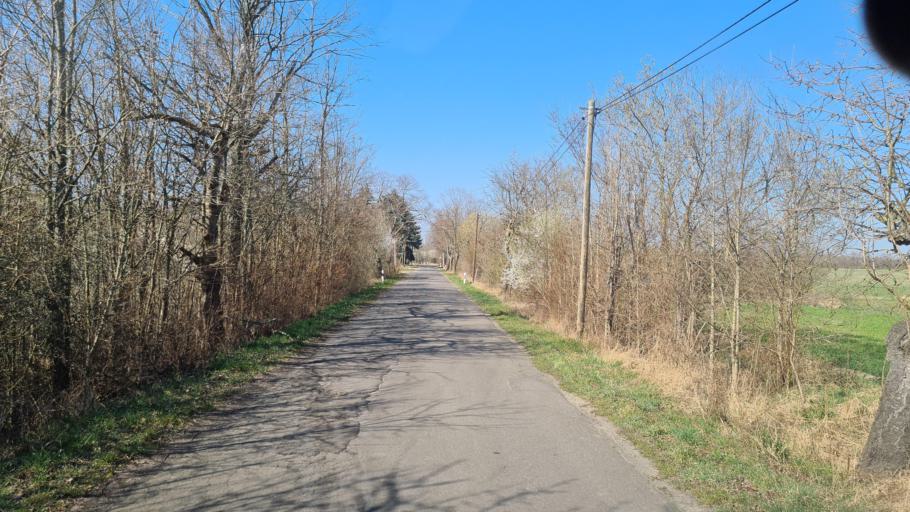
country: DE
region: Brandenburg
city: Vetschau
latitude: 51.7884
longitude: 14.0092
